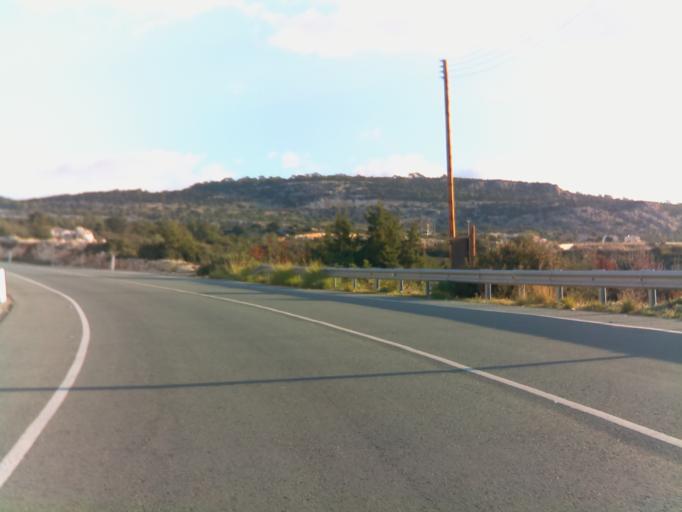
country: CY
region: Pafos
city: Pegeia
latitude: 34.8849
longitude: 32.3467
